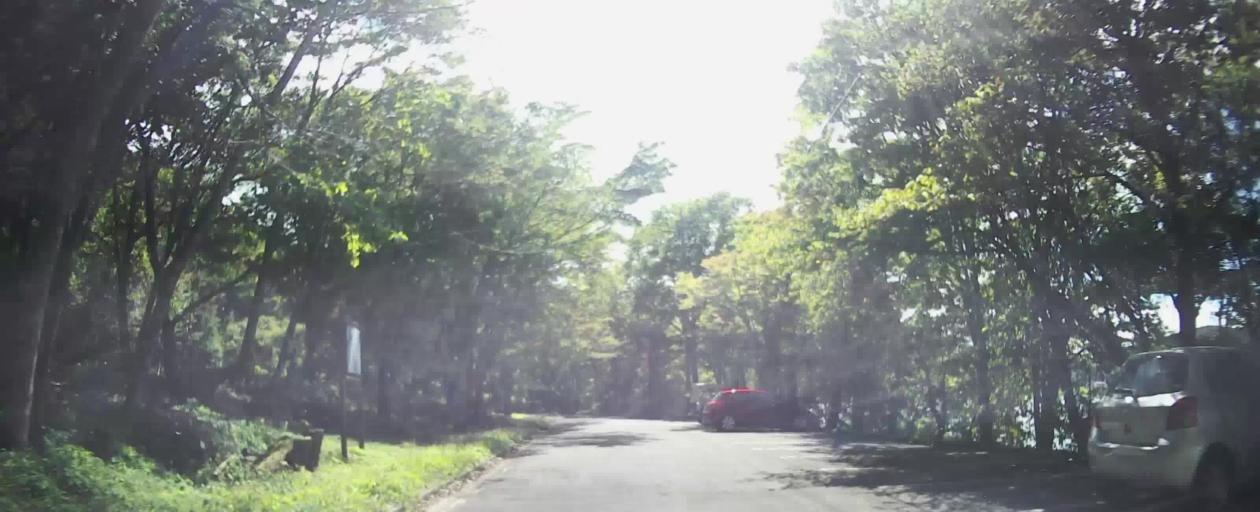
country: JP
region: Gunma
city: Nakanojomachi
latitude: 36.4780
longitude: 138.8718
